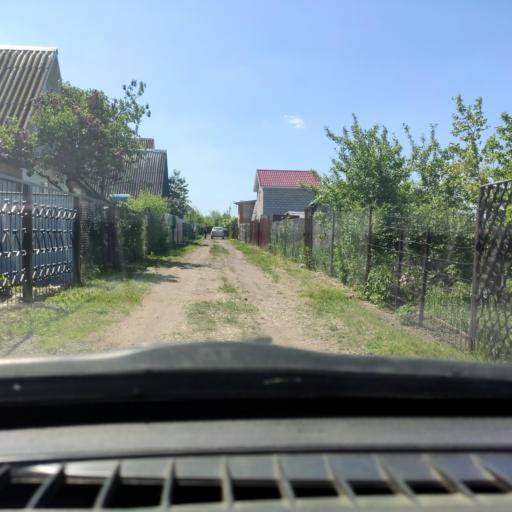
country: RU
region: Samara
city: Zhigulevsk
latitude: 53.5860
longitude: 49.5641
